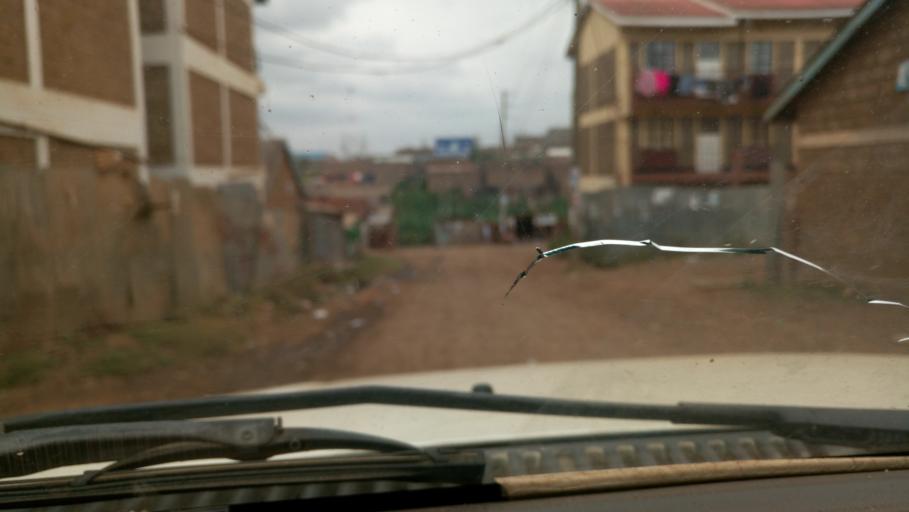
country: KE
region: Nairobi Area
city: Pumwani
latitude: -1.2435
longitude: 36.8921
